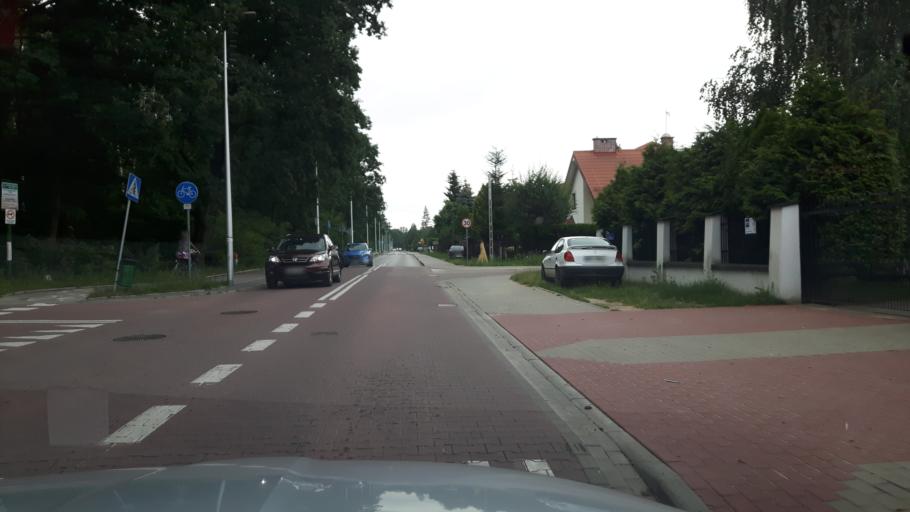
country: PL
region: Masovian Voivodeship
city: Zielonka
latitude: 52.2968
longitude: 21.1620
